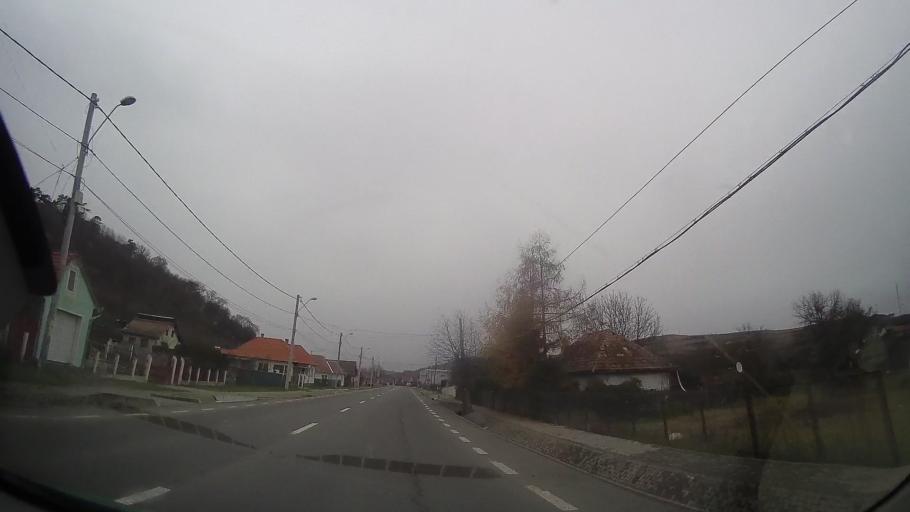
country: RO
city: Remetea
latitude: 46.5974
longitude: 24.5313
